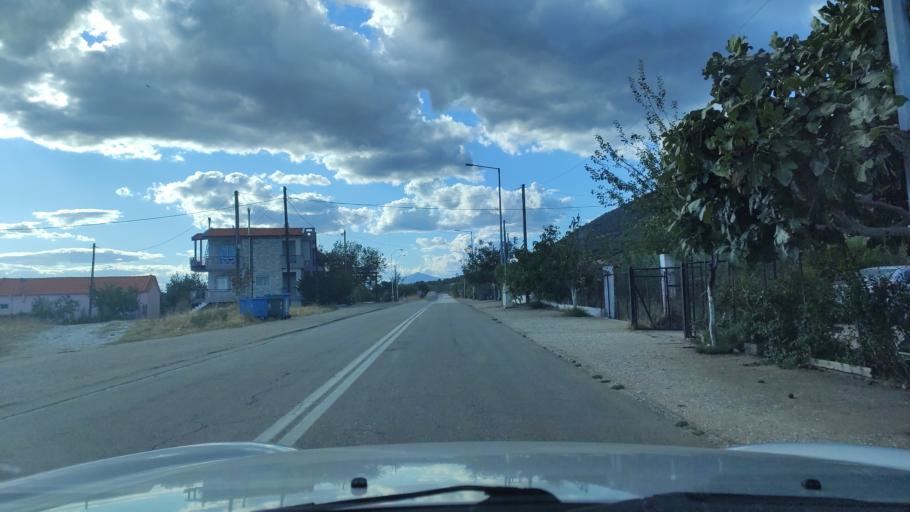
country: GR
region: East Macedonia and Thrace
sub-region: Nomos Rodopis
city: Iasmos
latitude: 41.1176
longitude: 25.1202
